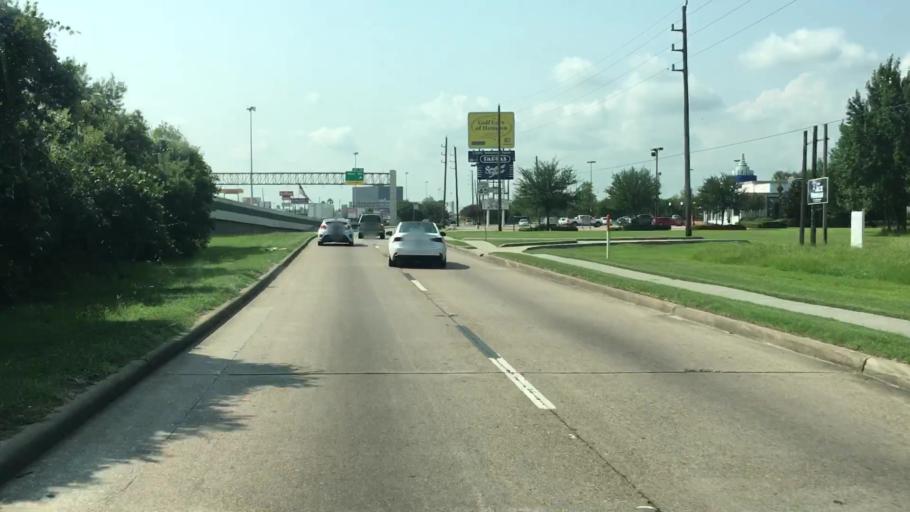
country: US
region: Texas
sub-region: Harris County
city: Aldine
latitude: 29.9311
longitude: -95.4123
